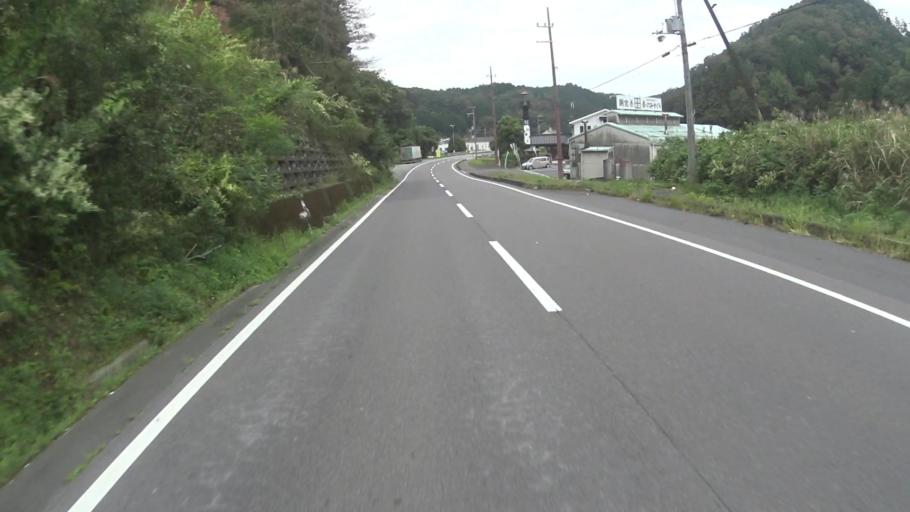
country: JP
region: Shiga Prefecture
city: Kusatsu
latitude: 34.8521
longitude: 135.9784
